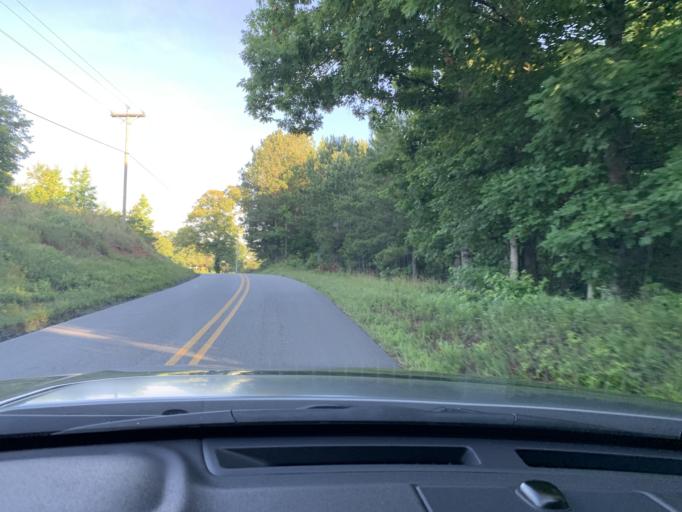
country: US
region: Georgia
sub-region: Bartow County
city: Rydal
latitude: 34.2585
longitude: -84.6960
